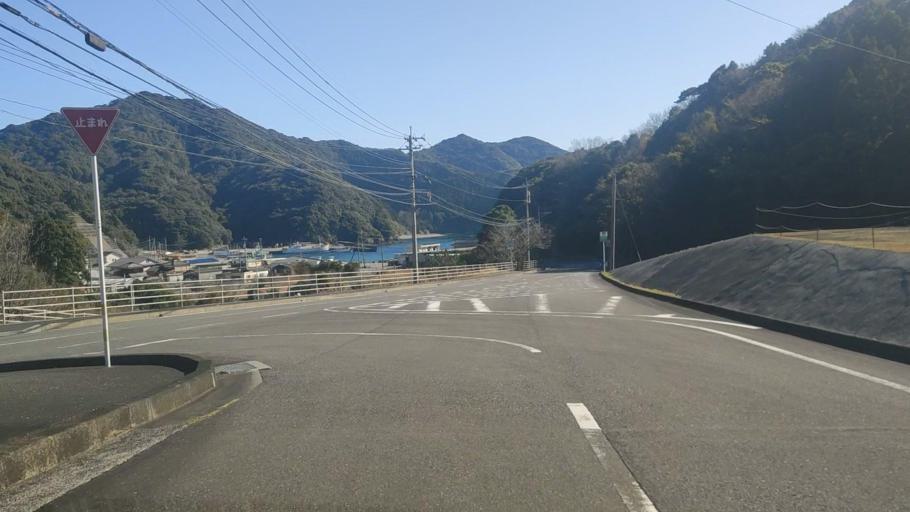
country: JP
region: Oita
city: Saiki
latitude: 32.7941
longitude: 131.9028
